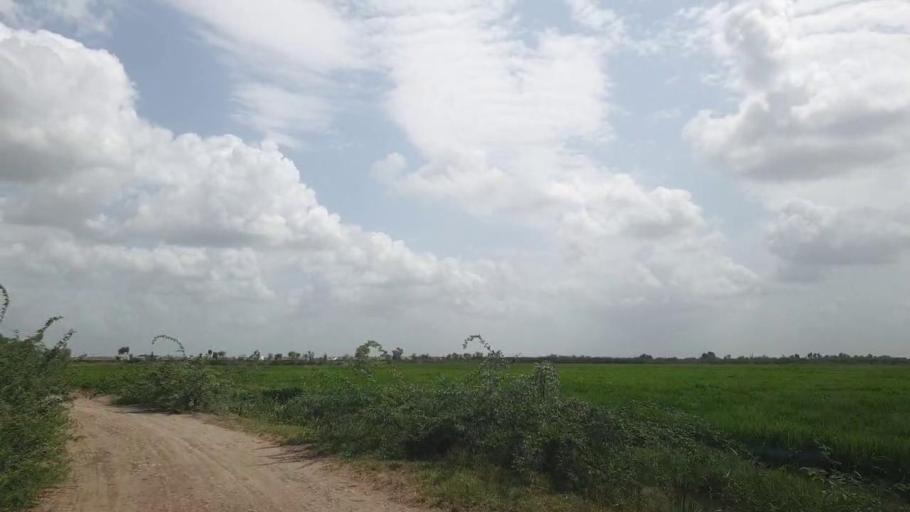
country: PK
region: Sindh
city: Tando Bago
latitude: 24.6537
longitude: 68.9981
